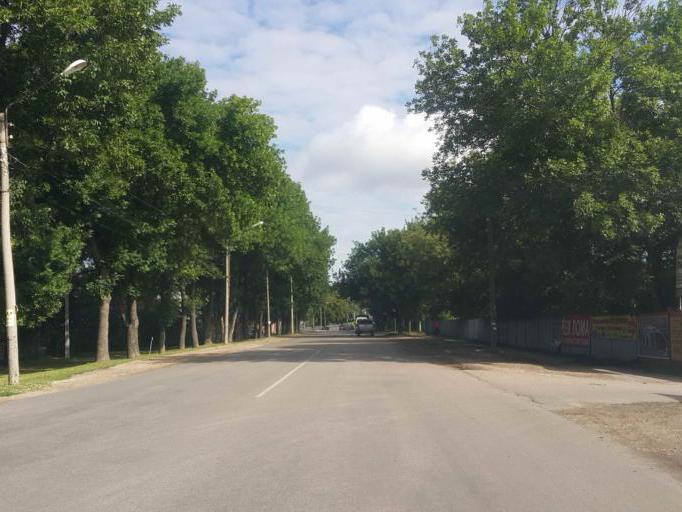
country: RU
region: Tambov
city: Tambov
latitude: 52.7171
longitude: 41.4247
